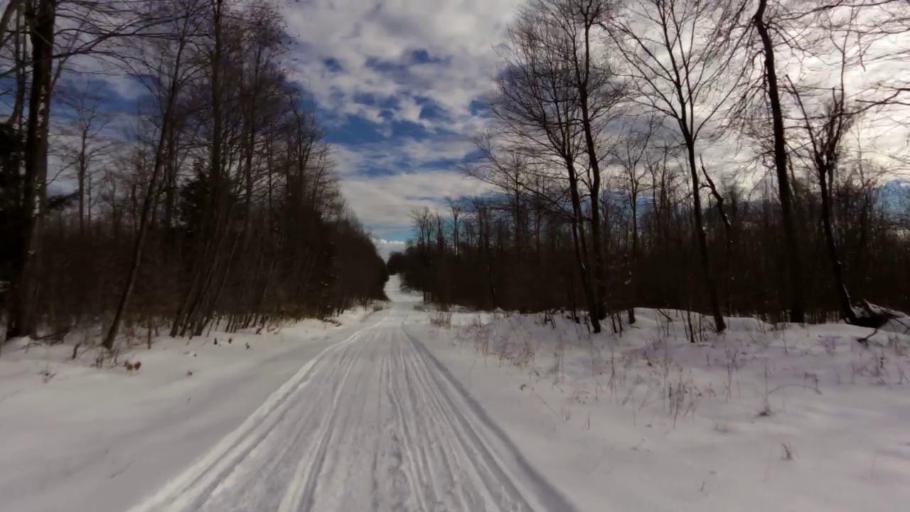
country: US
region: Pennsylvania
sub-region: McKean County
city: Foster Brook
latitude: 42.0168
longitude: -78.5495
